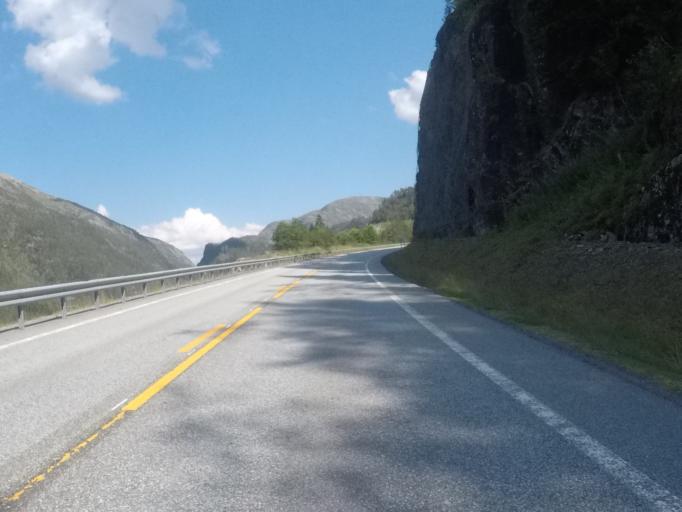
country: NO
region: Hordaland
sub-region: Modalen
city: Mo
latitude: 60.7748
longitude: 5.6230
